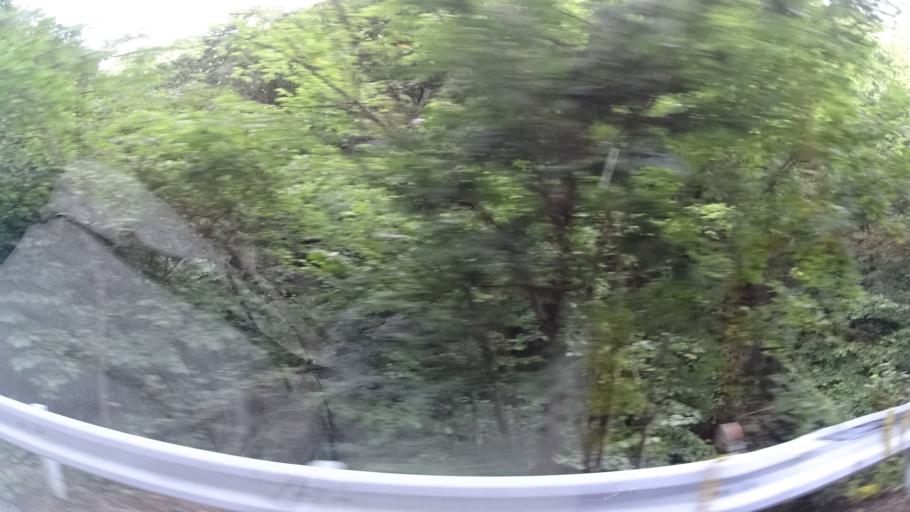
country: JP
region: Tochigi
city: Nikko
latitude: 36.6979
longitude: 139.5057
